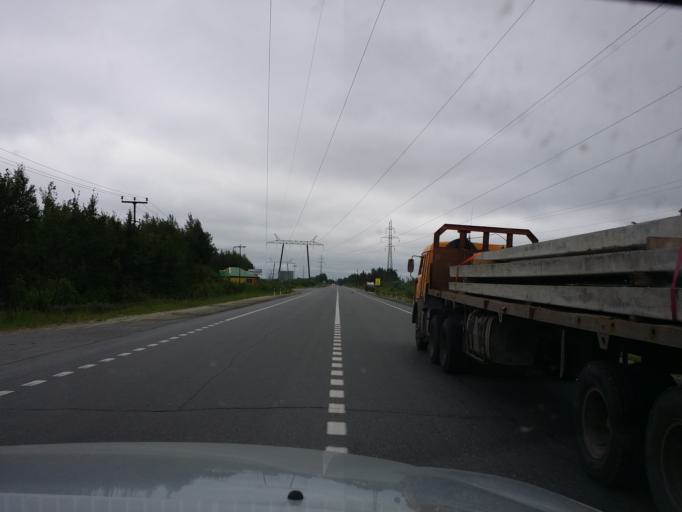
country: RU
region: Khanty-Mansiyskiy Avtonomnyy Okrug
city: Nizhnevartovsk
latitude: 61.0326
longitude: 76.3603
